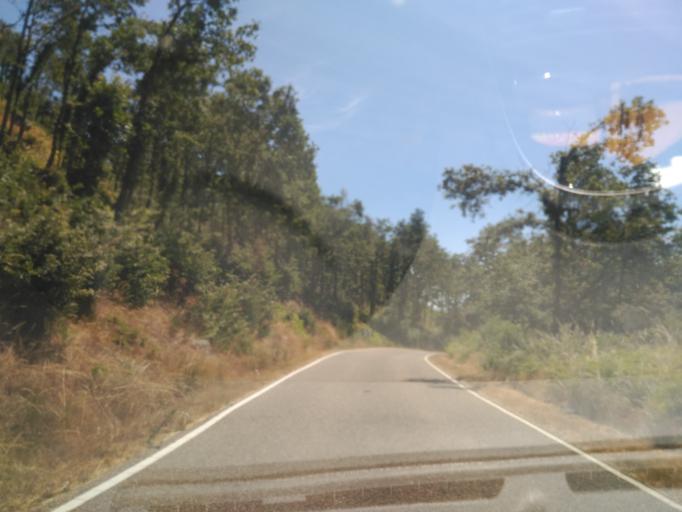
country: ES
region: Castille and Leon
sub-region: Provincia de Zamora
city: Galende
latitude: 42.1351
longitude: -6.7144
